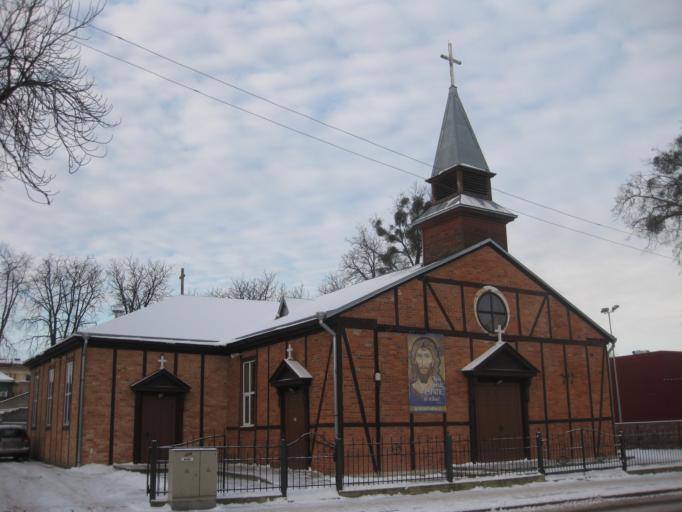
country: LT
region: Kauno apskritis
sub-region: Kaunas
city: Kaunas
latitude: 54.9052
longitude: 23.9214
